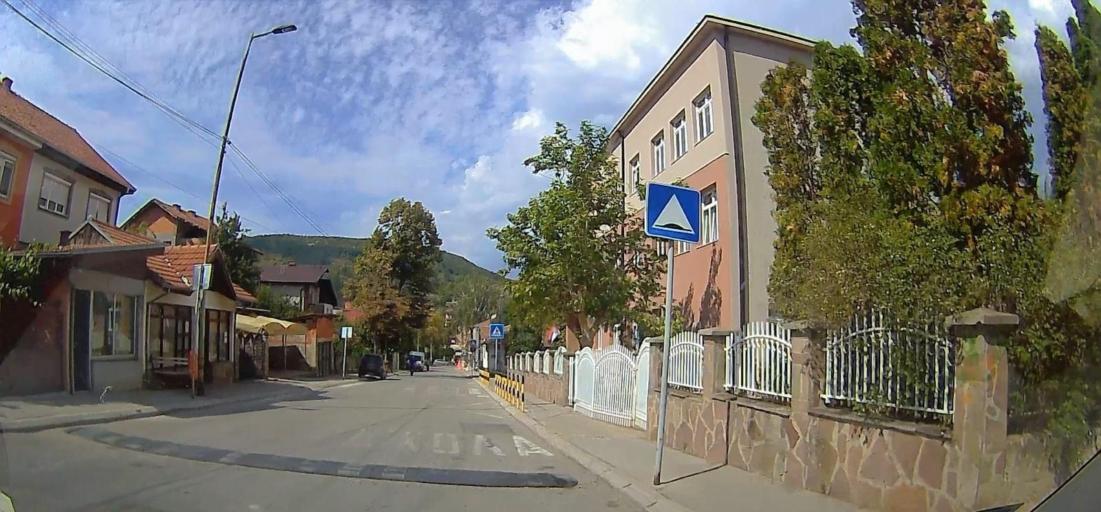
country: RS
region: Central Serbia
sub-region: Pirotski Okrug
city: Dimitrovgrad
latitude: 43.0146
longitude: 22.7791
